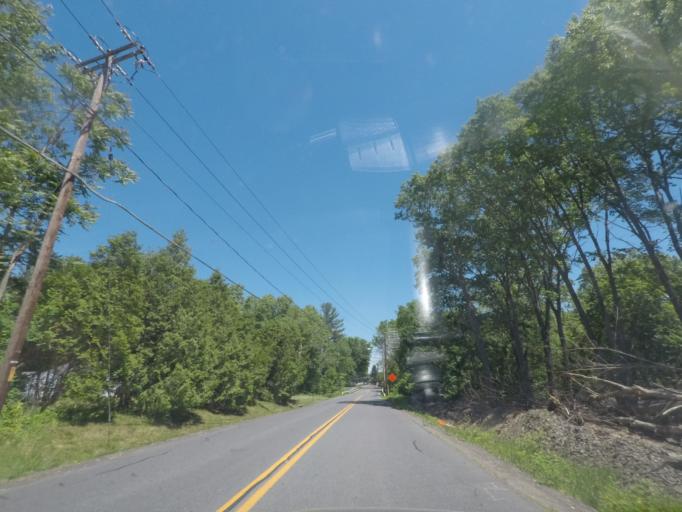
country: US
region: New York
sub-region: Saratoga County
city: Stillwater
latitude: 42.9389
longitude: -73.6610
